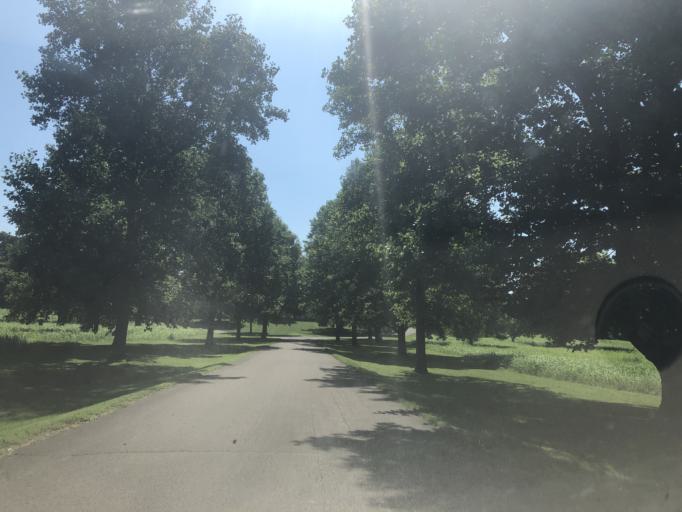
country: US
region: Tennessee
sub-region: Davidson County
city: Lakewood
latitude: 36.2125
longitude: -86.6054
